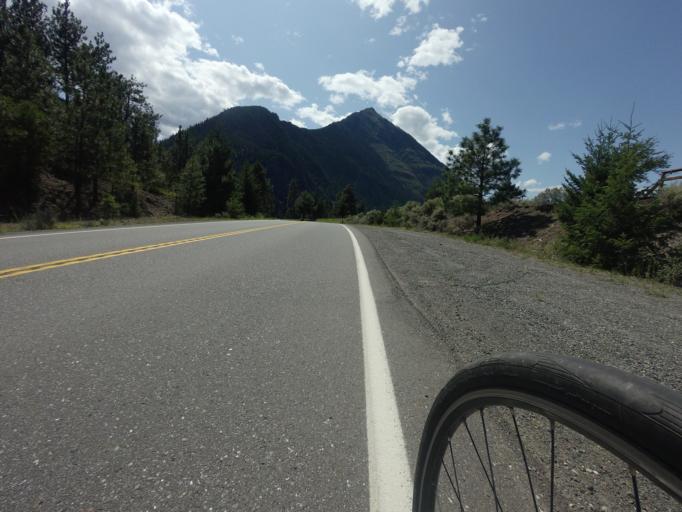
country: CA
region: British Columbia
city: Lillooet
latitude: 50.6684
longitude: -121.9852
